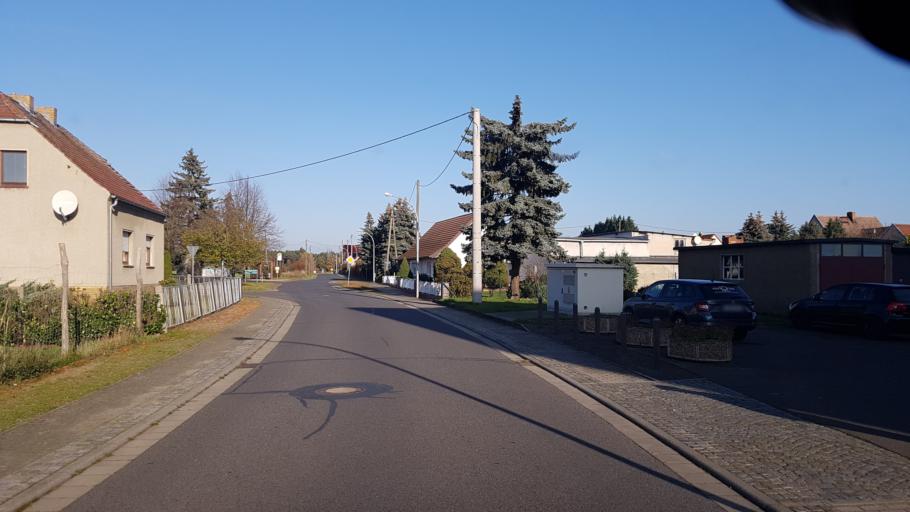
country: DE
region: Brandenburg
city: Schipkau
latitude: 51.5687
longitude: 13.9232
